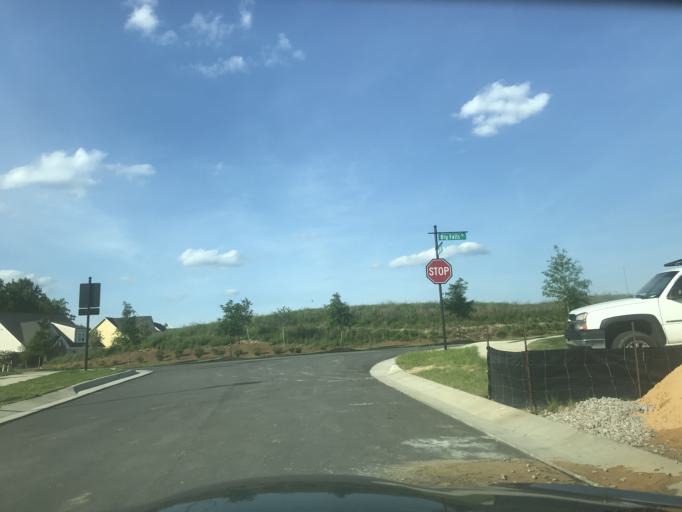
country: US
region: North Carolina
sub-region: Wake County
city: Knightdale
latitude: 35.7673
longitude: -78.4308
